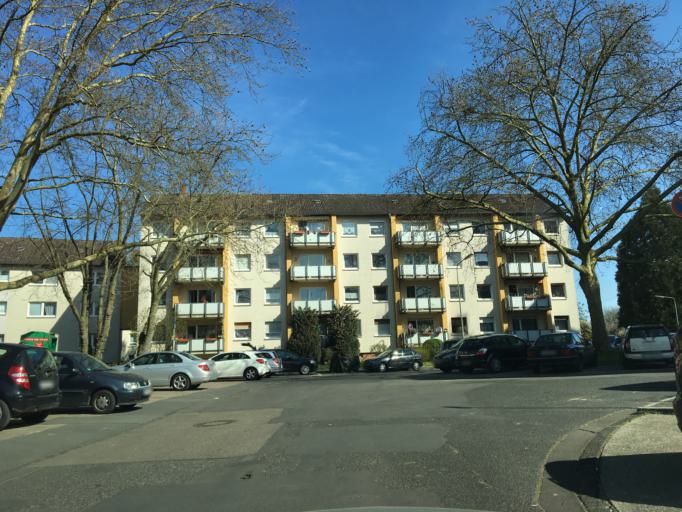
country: DE
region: Hesse
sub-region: Regierungsbezirk Darmstadt
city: Frankfurt am Main
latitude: 50.1662
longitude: 8.6598
